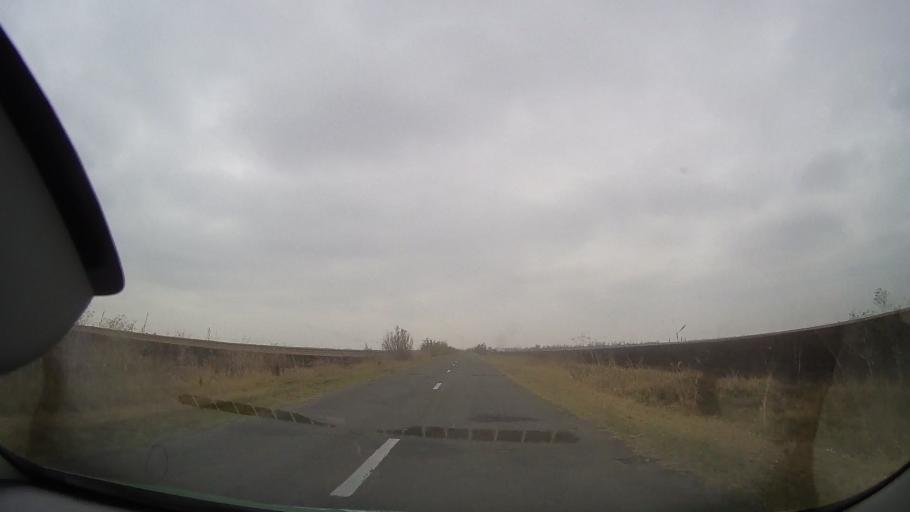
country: RO
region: Ialomita
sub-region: Comuna Valea Macrisului
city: Valea Macrisului
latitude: 44.7587
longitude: 26.8032
